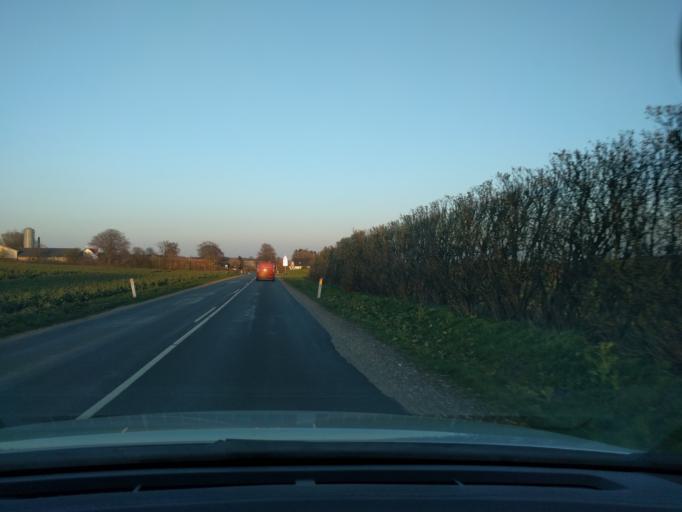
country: DK
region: South Denmark
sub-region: Assens Kommune
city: Glamsbjerg
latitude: 55.2716
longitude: 10.0581
